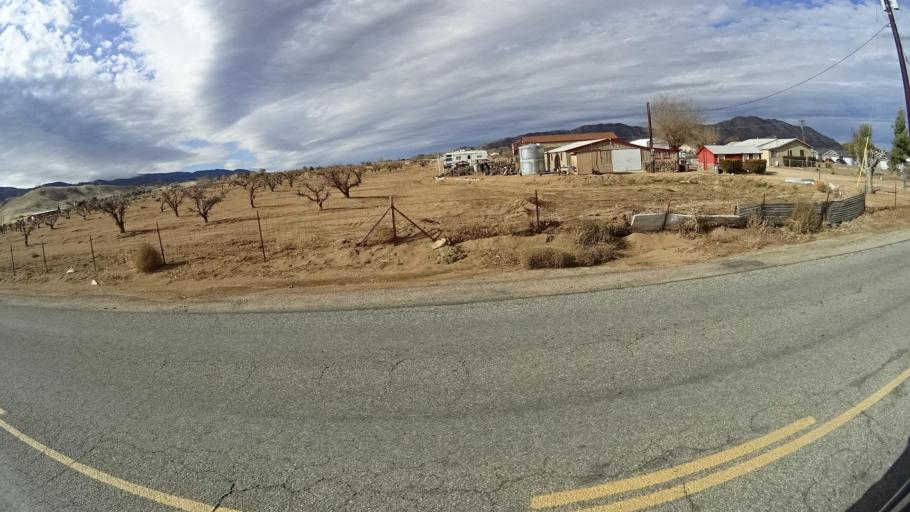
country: US
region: California
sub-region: Kern County
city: Tehachapi
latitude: 35.1195
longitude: -118.4674
